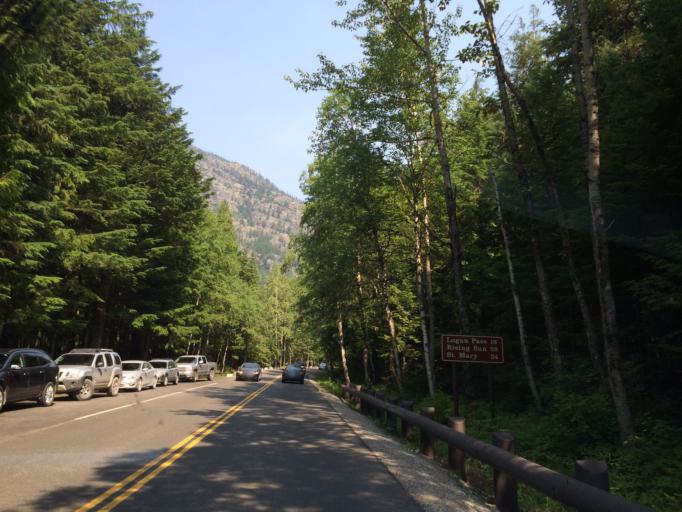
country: US
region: Montana
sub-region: Flathead County
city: Columbia Falls
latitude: 48.6823
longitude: -113.8197
